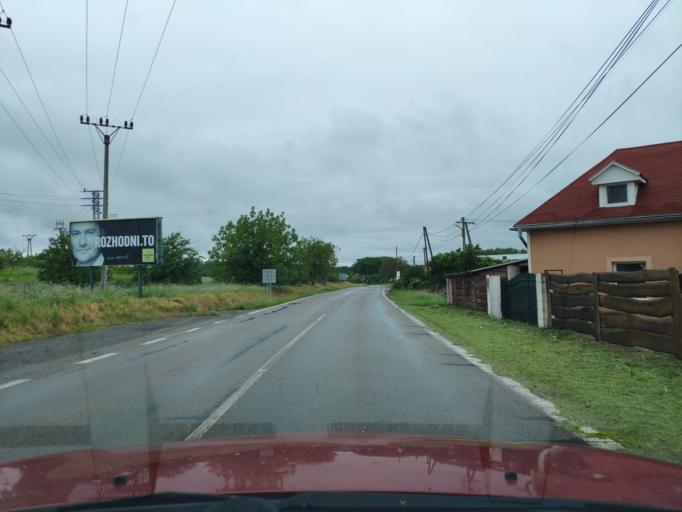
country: HU
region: Borsod-Abauj-Zemplen
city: Ricse
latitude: 48.4326
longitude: 21.9677
